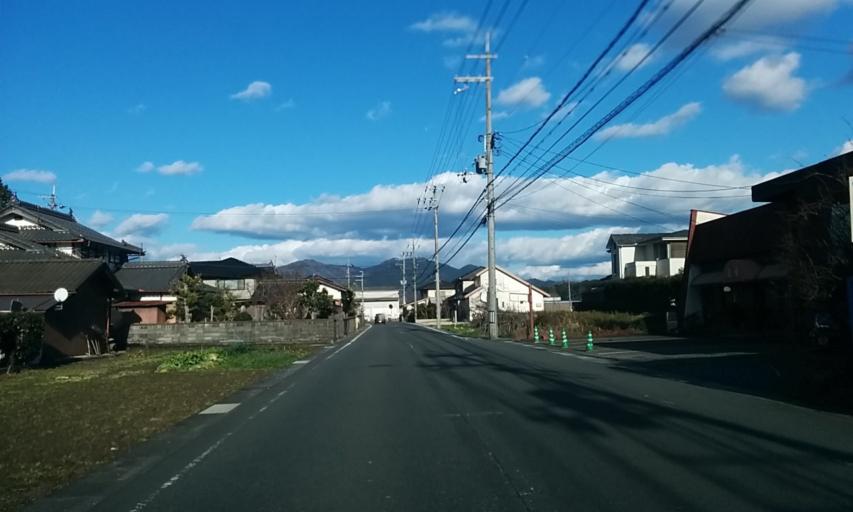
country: JP
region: Kyoto
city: Fukuchiyama
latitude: 35.2967
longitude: 135.0912
